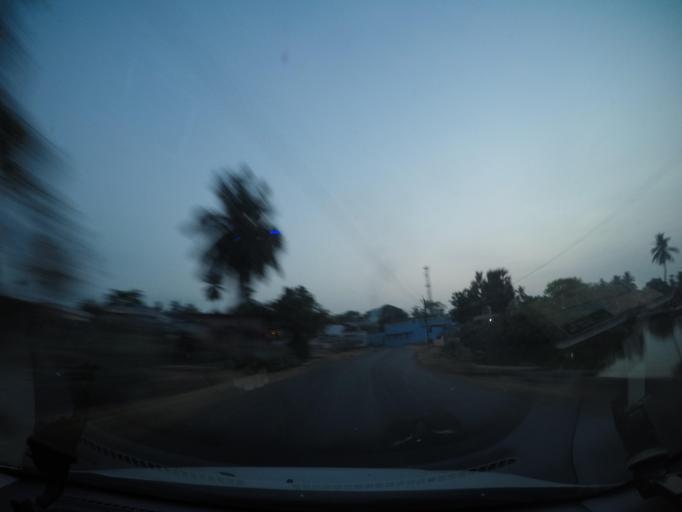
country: IN
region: Andhra Pradesh
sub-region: West Godavari
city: Tadepallegudem
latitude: 16.7809
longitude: 81.4246
